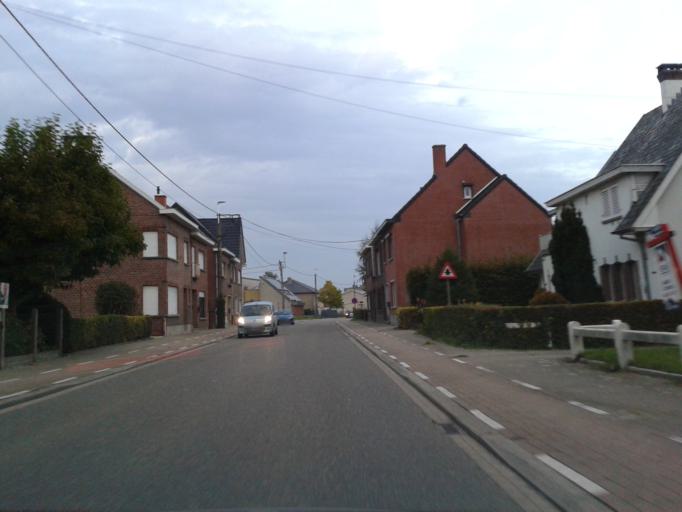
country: BE
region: Flanders
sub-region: Provincie Oost-Vlaanderen
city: Lebbeke
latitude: 50.9949
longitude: 4.1172
